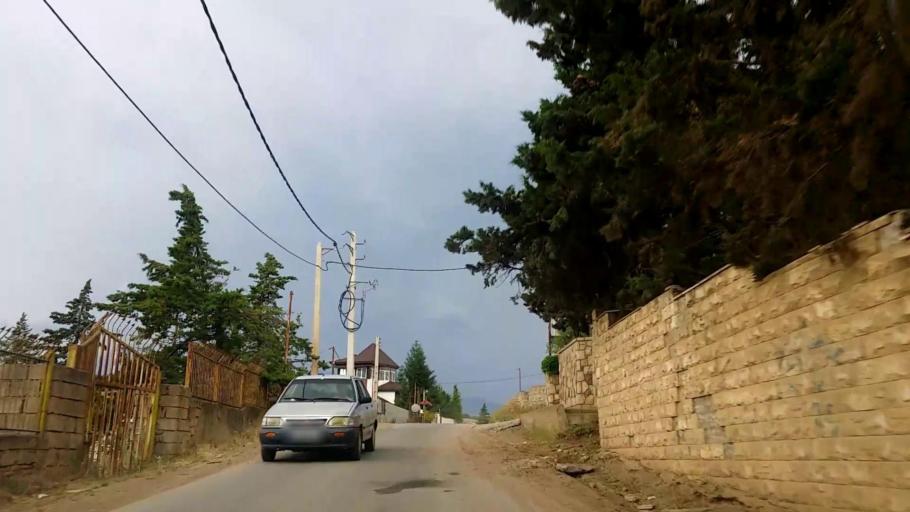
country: IR
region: Mazandaran
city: Chalus
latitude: 36.5155
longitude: 51.2501
